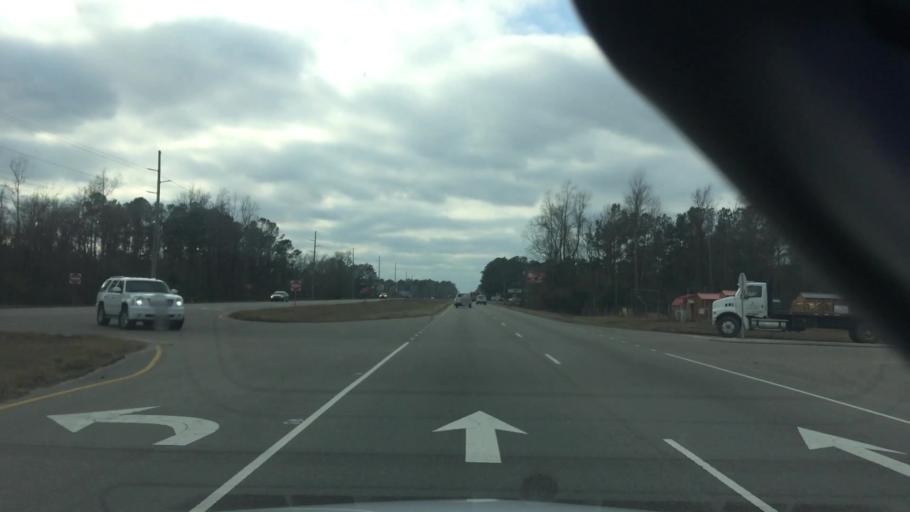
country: US
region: North Carolina
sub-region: Brunswick County
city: Shallotte
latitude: 33.9895
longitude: -78.3531
